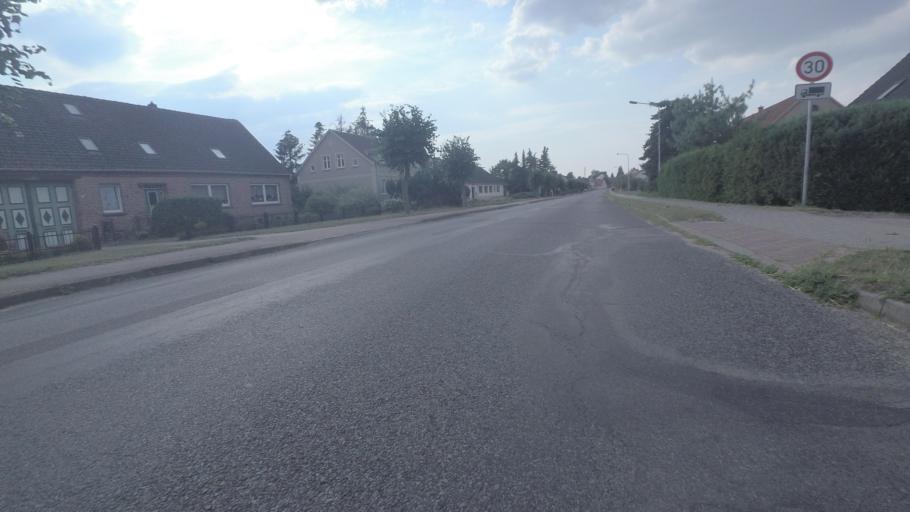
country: DE
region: Brandenburg
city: Wittstock
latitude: 53.2437
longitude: 12.4206
